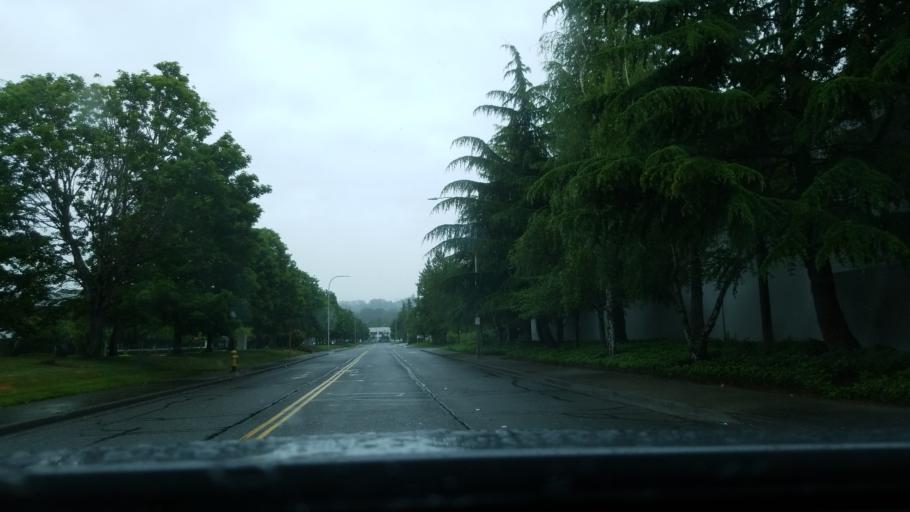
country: US
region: Washington
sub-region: King County
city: Renton
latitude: 47.4456
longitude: -122.2292
